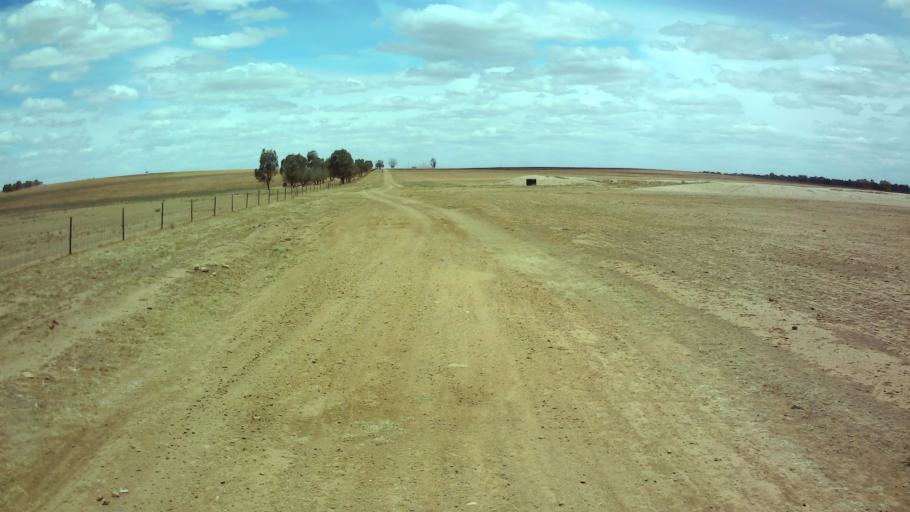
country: AU
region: New South Wales
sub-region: Weddin
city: Grenfell
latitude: -33.8924
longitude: 147.7409
